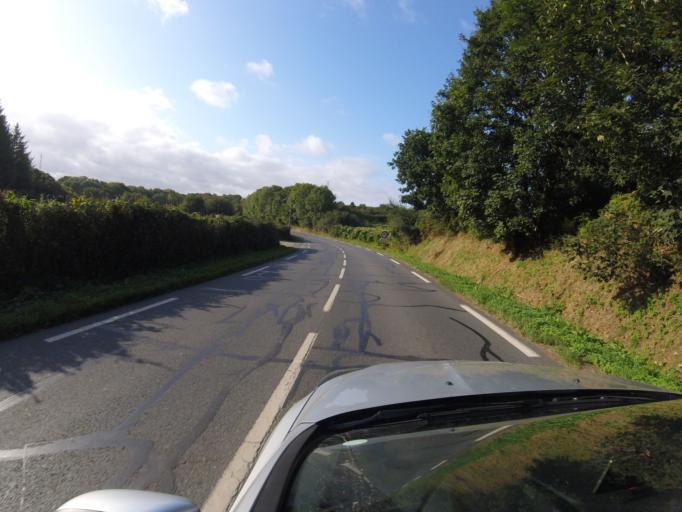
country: FR
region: Haute-Normandie
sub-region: Departement de la Seine-Maritime
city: Fecamp
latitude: 49.7666
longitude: 0.4047
